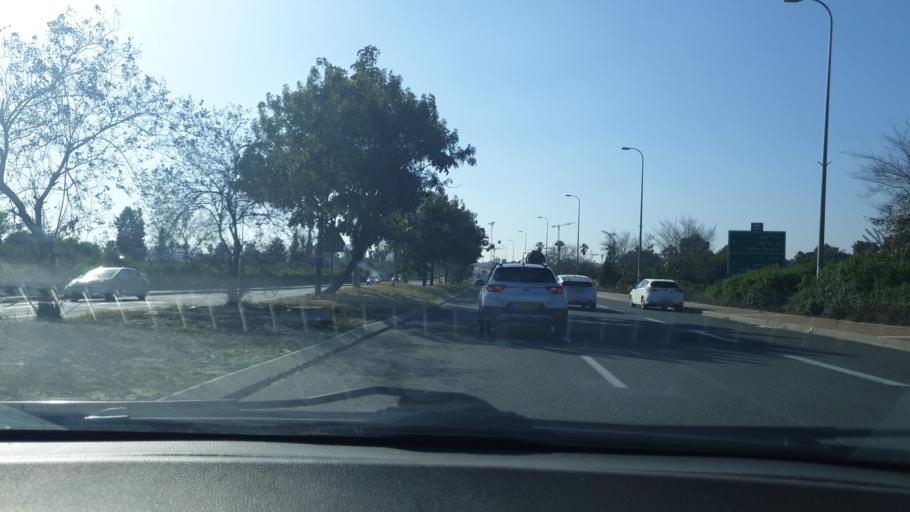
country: IL
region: Central District
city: Ramla
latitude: 31.9515
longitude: 34.8554
